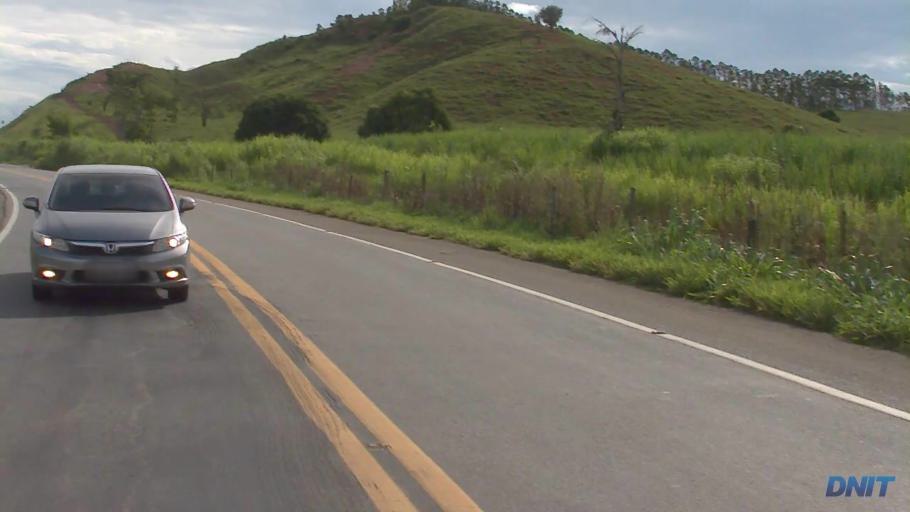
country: BR
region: Minas Gerais
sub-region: Belo Oriente
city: Belo Oriente
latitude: -19.1841
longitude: -42.2637
